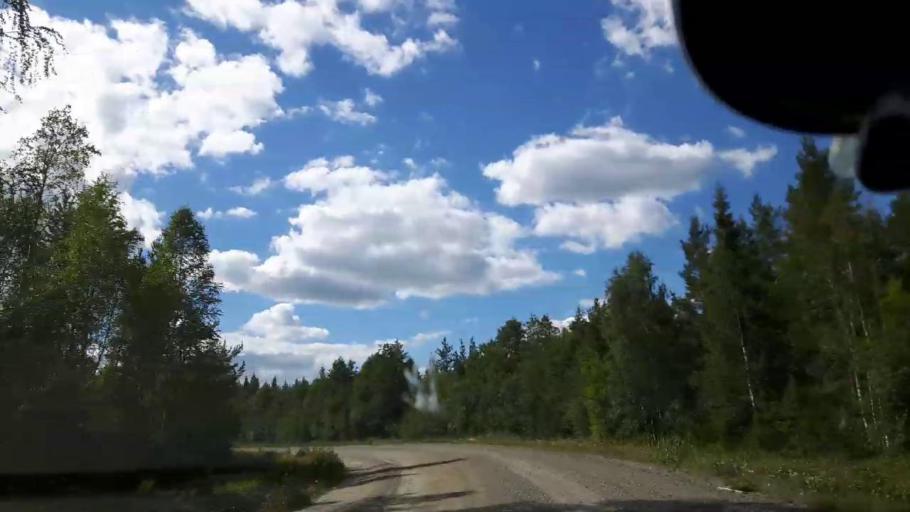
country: SE
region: Vaesternorrland
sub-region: Ange Kommun
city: Ange
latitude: 62.7723
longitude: 15.9204
